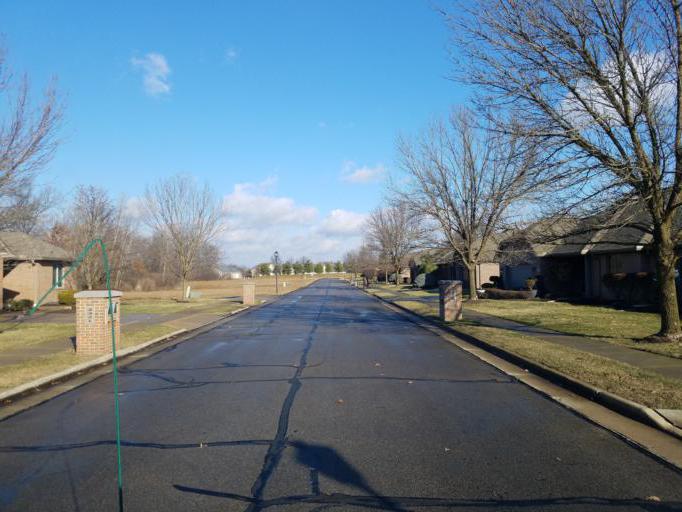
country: US
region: Ohio
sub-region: Marion County
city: Marion
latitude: 40.5439
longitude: -83.1596
